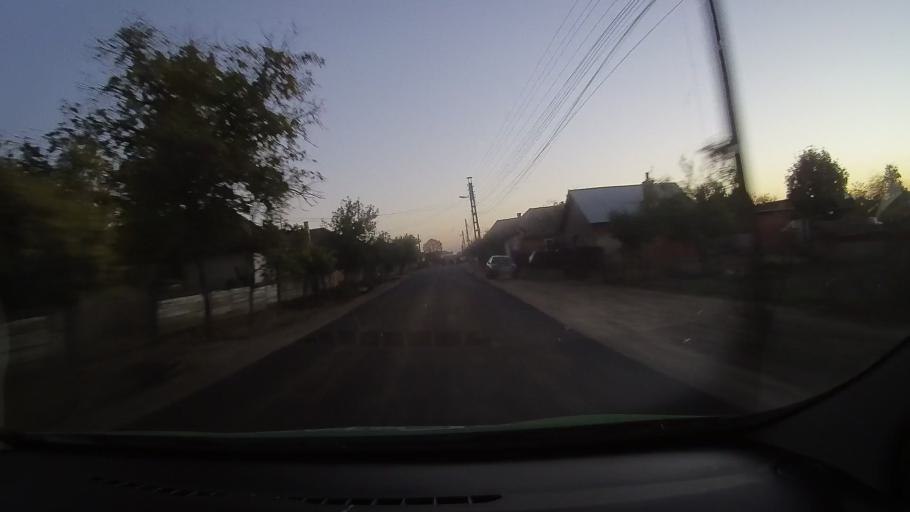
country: RO
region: Bihor
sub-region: Comuna Simian
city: Simian
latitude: 47.5025
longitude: 22.0919
